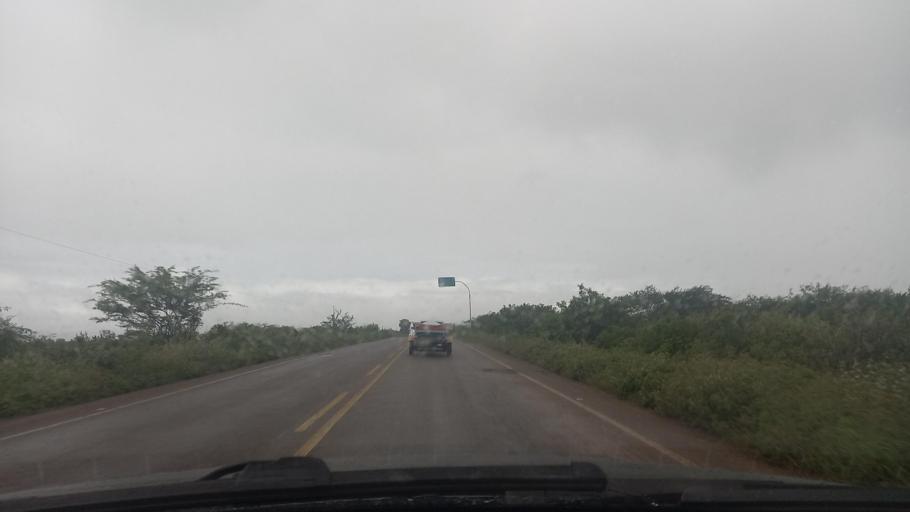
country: BR
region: Bahia
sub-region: Paulo Afonso
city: Paulo Afonso
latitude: -9.3547
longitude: -38.2775
